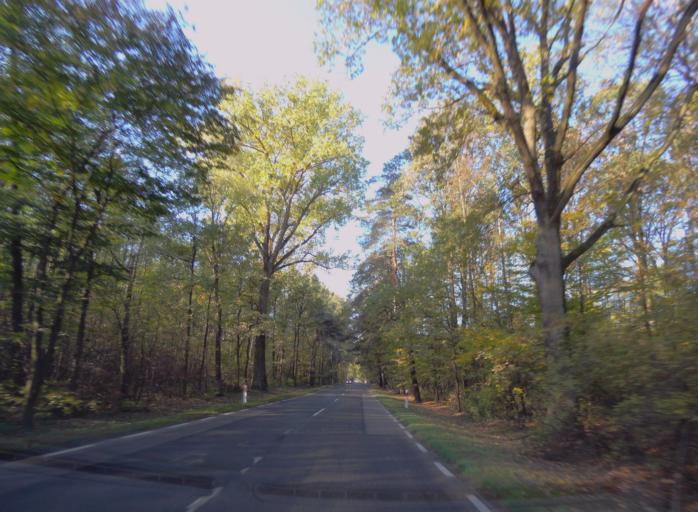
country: PL
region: Masovian Voivodeship
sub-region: Powiat siedlecki
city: Mordy
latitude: 52.1958
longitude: 22.4815
